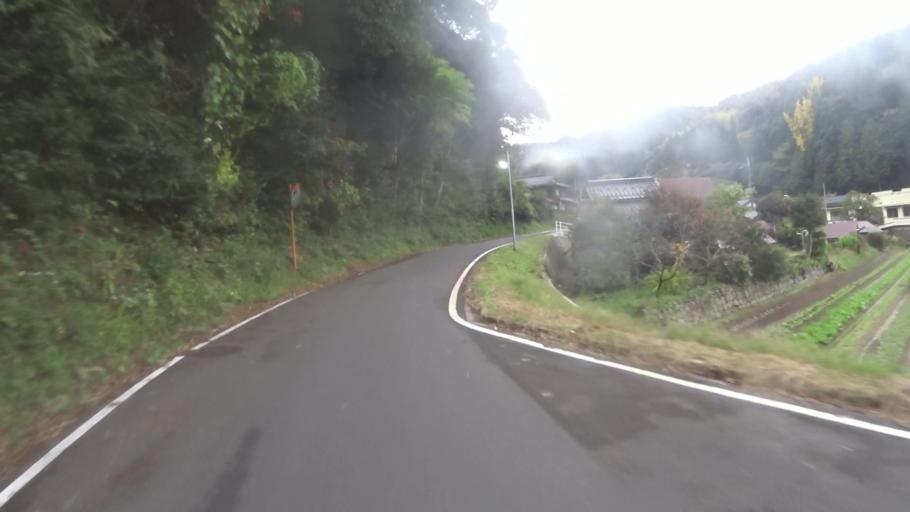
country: JP
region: Kyoto
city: Miyazu
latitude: 35.5340
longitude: 135.2144
